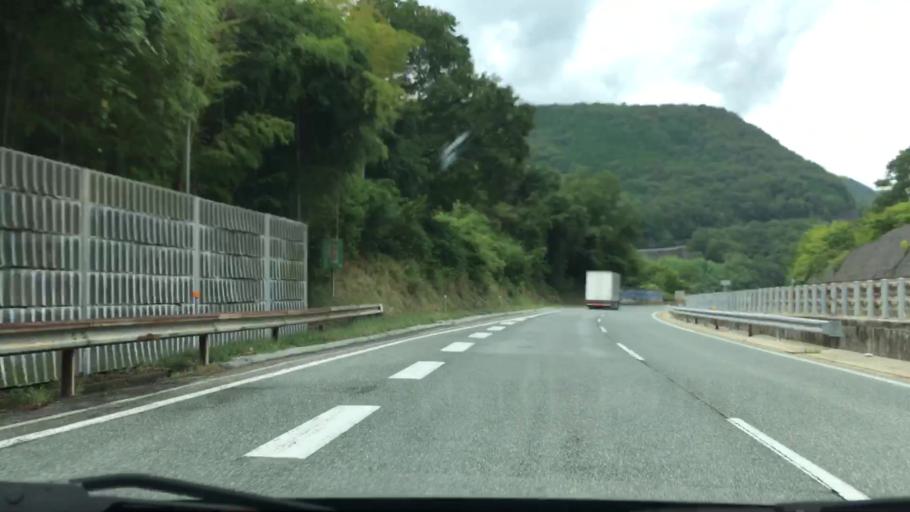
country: JP
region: Okayama
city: Niimi
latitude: 34.9659
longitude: 133.6305
